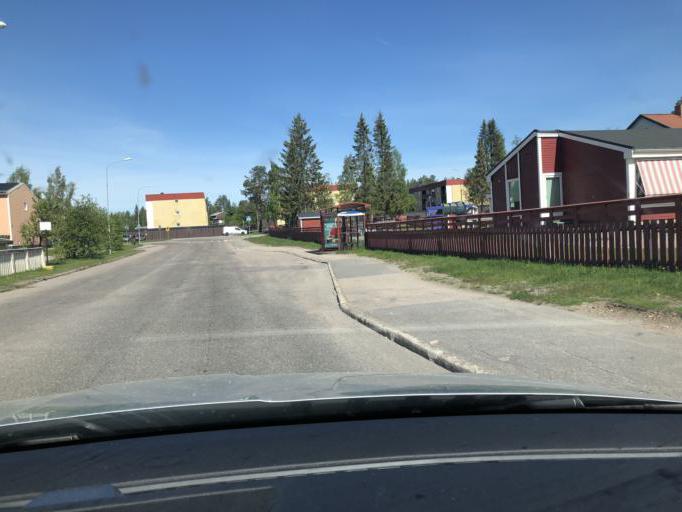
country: SE
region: Norrbotten
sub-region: Gallivare Kommun
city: Gaellivare
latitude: 67.1329
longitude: 20.6820
